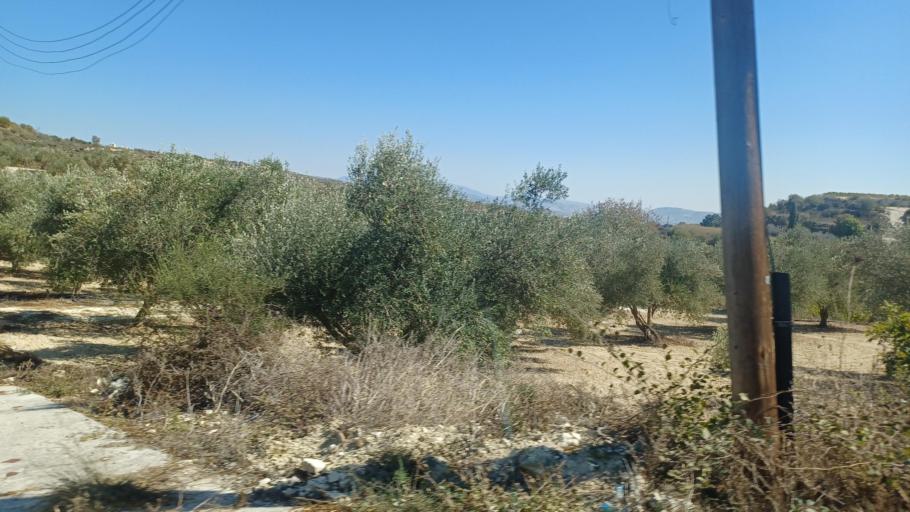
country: CY
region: Pafos
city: Mesogi
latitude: 34.8261
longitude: 32.4796
